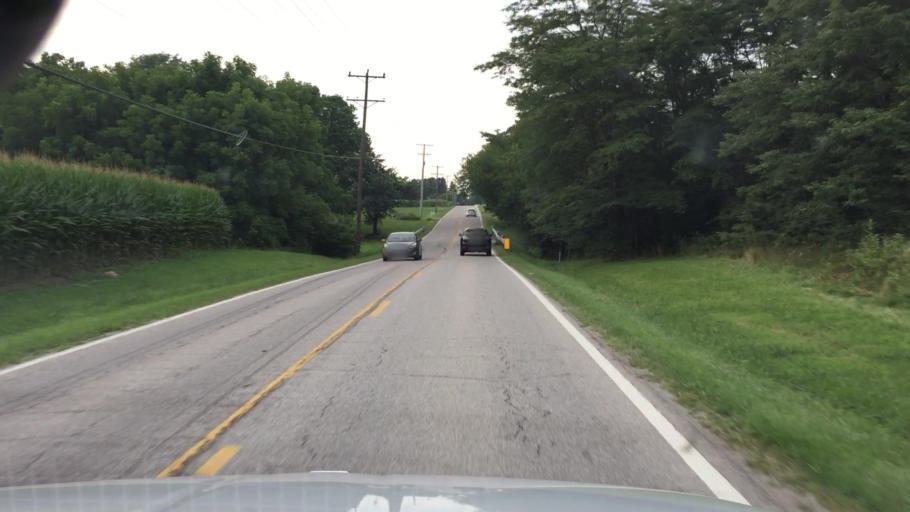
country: US
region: Ohio
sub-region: Madison County
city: Plain City
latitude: 40.0366
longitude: -83.2630
